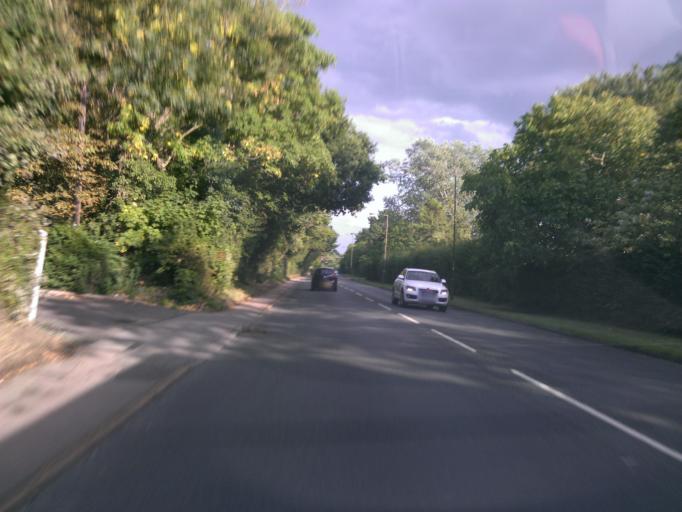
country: GB
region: England
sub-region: Kent
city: Tonbridge
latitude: 51.2120
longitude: 0.2521
